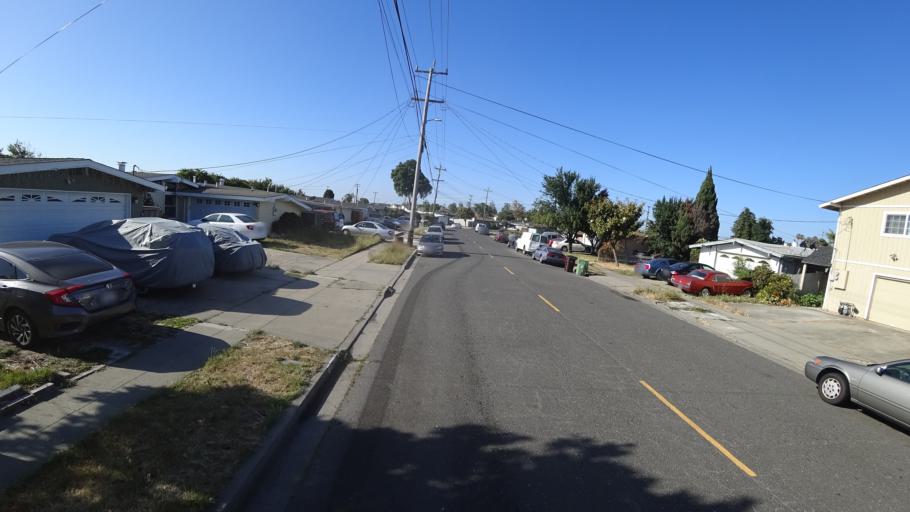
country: US
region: California
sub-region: Alameda County
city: Hayward
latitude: 37.6260
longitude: -122.1014
